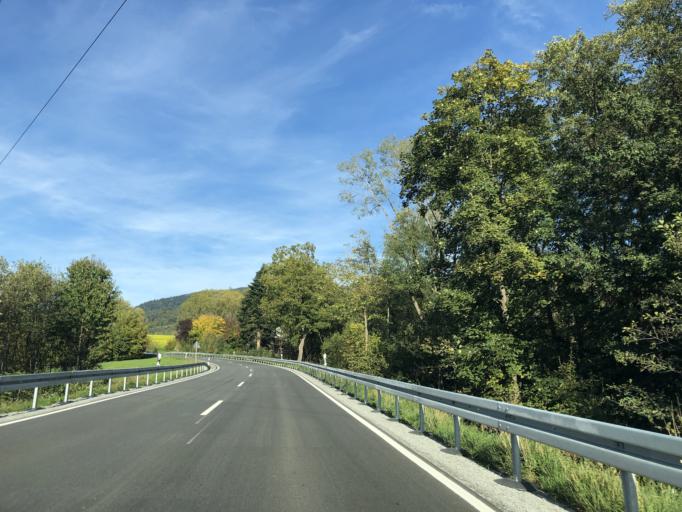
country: DE
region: Bavaria
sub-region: Lower Bavaria
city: Grafling
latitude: 48.8865
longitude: 12.9678
